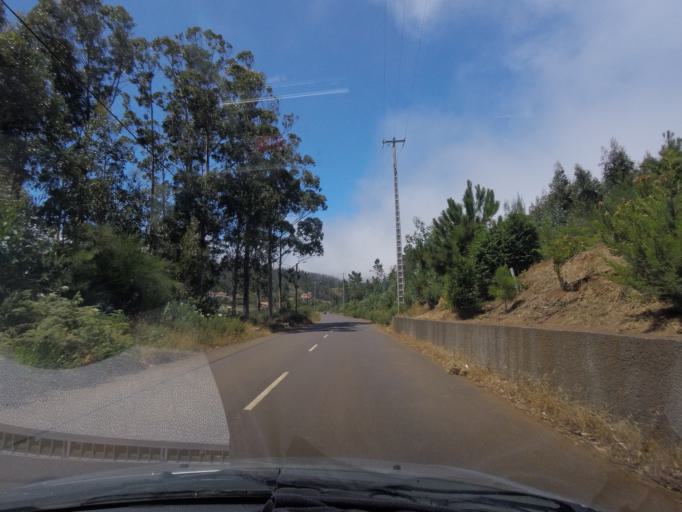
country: PT
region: Madeira
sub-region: Santa Cruz
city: Camacha
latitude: 32.6921
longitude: -16.8341
